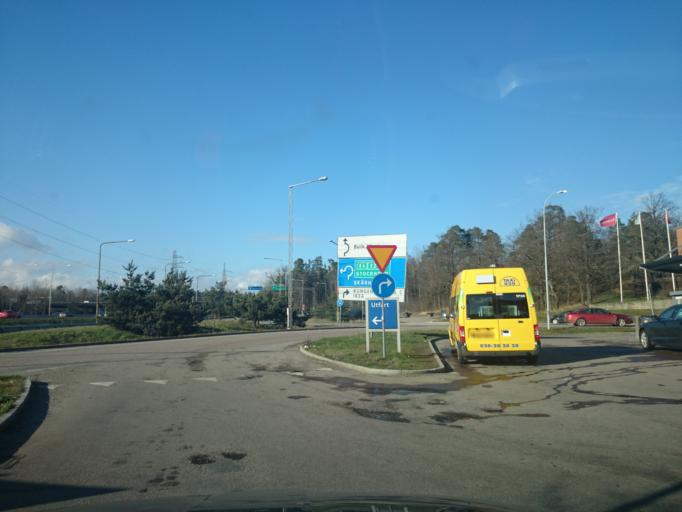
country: SE
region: Stockholm
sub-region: Huddinge Kommun
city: Segeltorp
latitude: 59.2717
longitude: 17.9138
